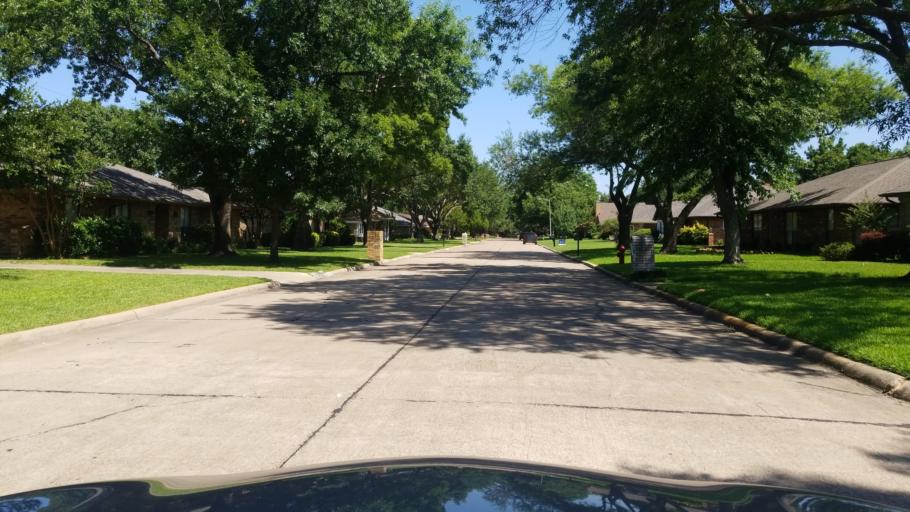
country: US
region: Texas
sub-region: Dallas County
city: Grand Prairie
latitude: 32.6919
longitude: -97.0007
